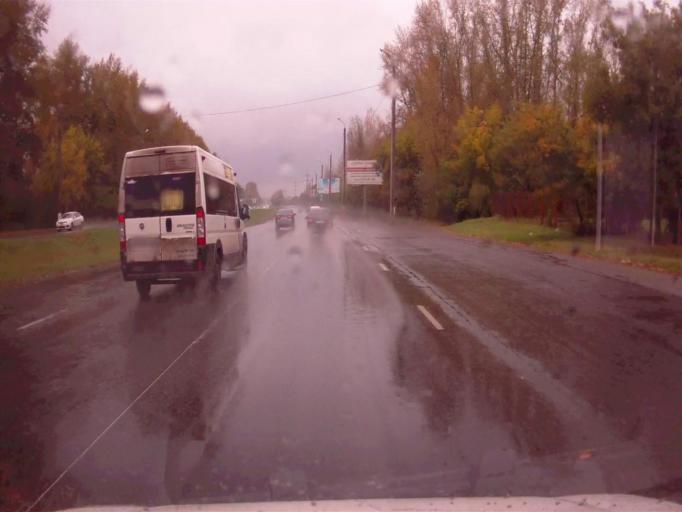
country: RU
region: Chelyabinsk
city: Dolgoderevenskoye
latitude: 55.2432
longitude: 61.3605
